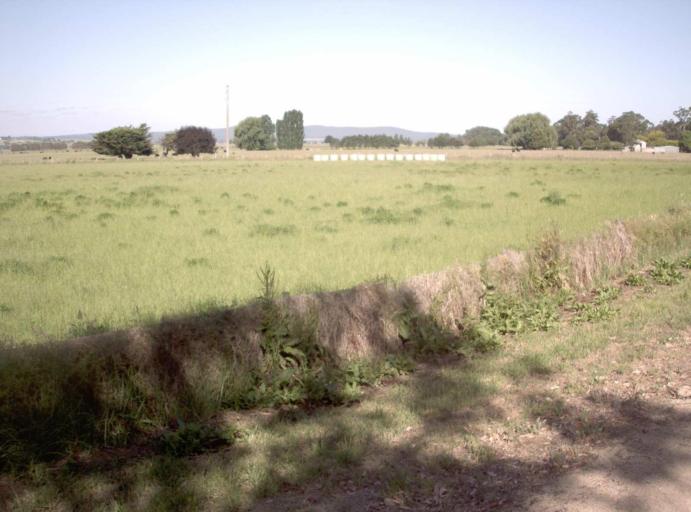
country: AU
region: Victoria
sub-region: East Gippsland
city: Lakes Entrance
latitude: -37.7166
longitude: 148.4568
